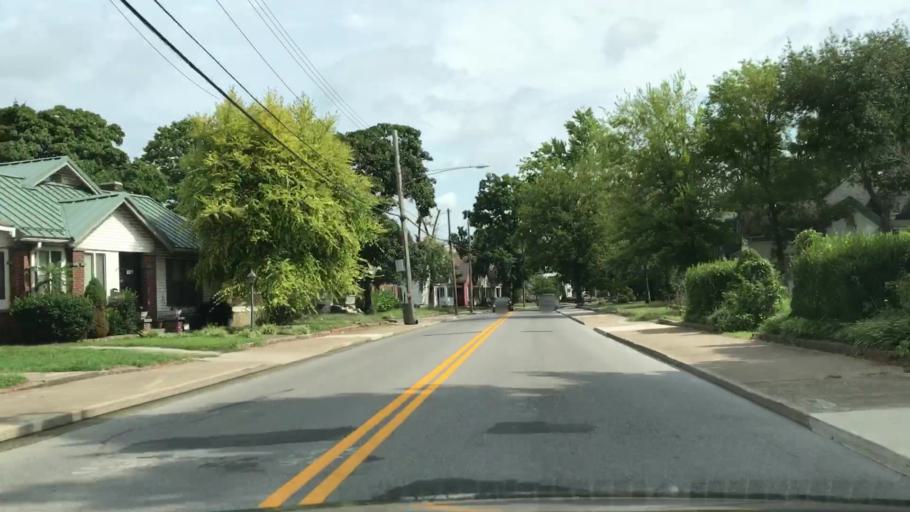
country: US
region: Kentucky
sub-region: Christian County
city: Hopkinsville
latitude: 36.8580
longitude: -87.4925
